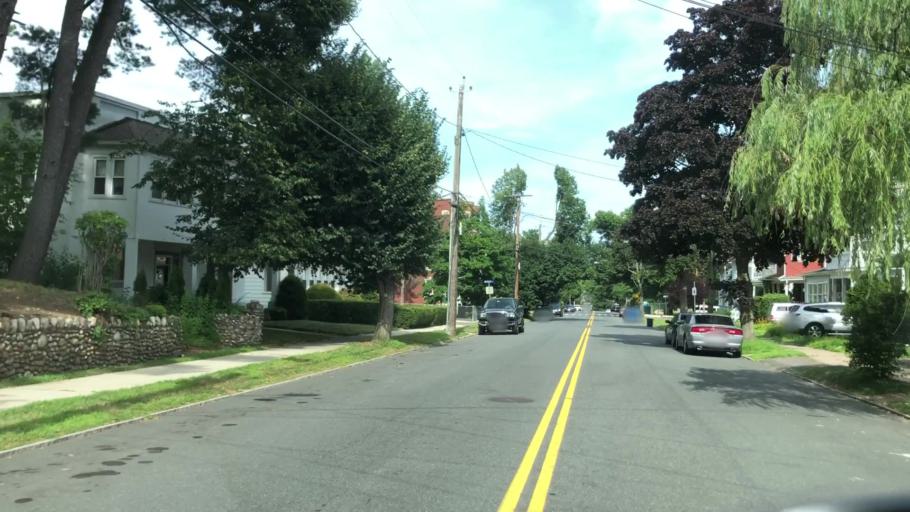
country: US
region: Massachusetts
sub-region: Hampden County
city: Holyoke
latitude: 42.2052
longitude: -72.6302
